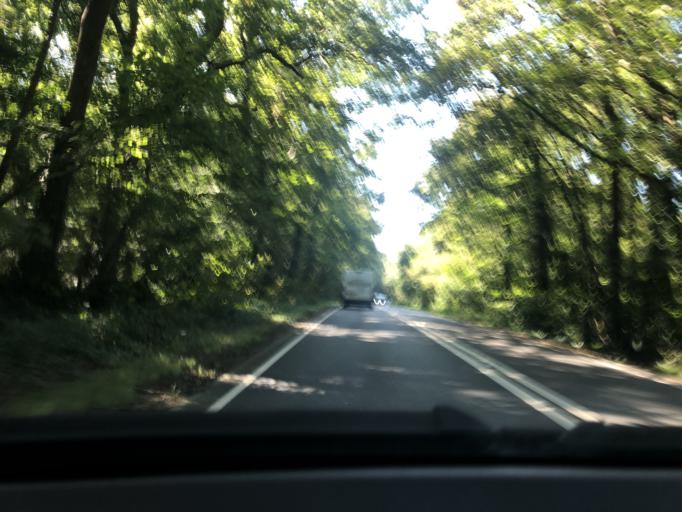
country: GB
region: England
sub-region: Somerset
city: Westonzoyland
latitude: 51.1325
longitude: -2.8470
